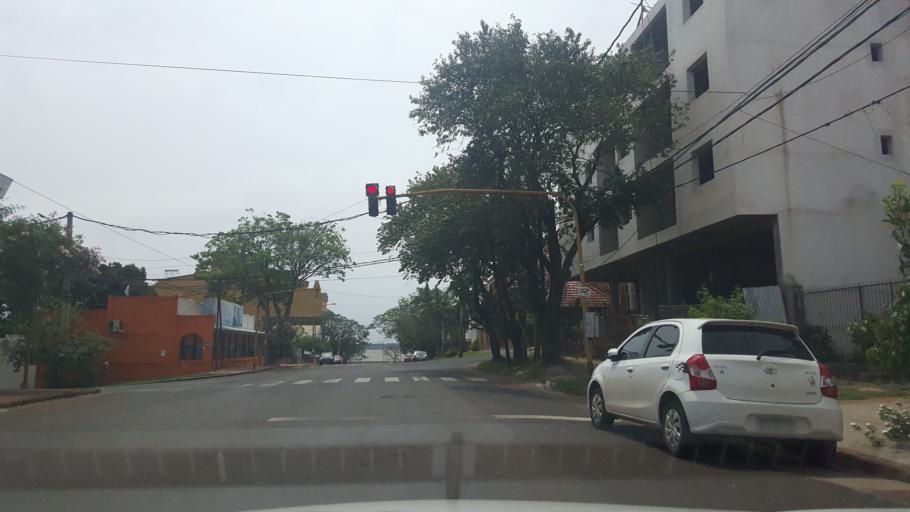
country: AR
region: Misiones
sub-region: Departamento de Capital
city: Posadas
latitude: -27.3542
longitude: -55.8995
